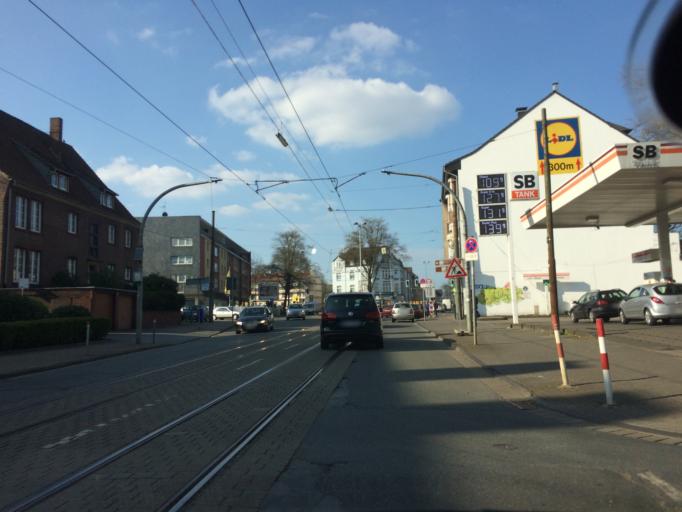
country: DE
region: North Rhine-Westphalia
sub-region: Regierungsbezirk Munster
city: Gelsenkirchen
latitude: 51.4923
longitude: 7.1230
